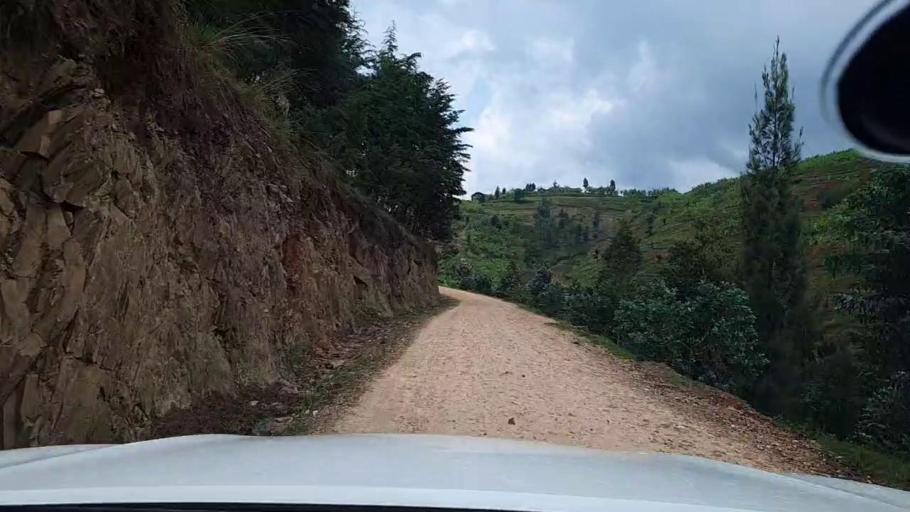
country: RW
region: Western Province
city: Kibuye
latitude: -2.1251
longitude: 29.4267
